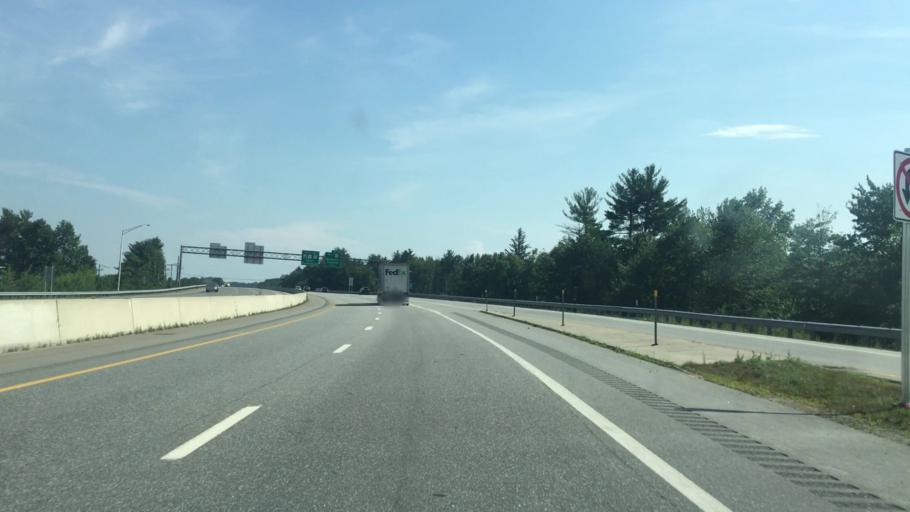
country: US
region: New Hampshire
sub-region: Strafford County
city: Rochester
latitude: 43.3161
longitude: -70.9967
